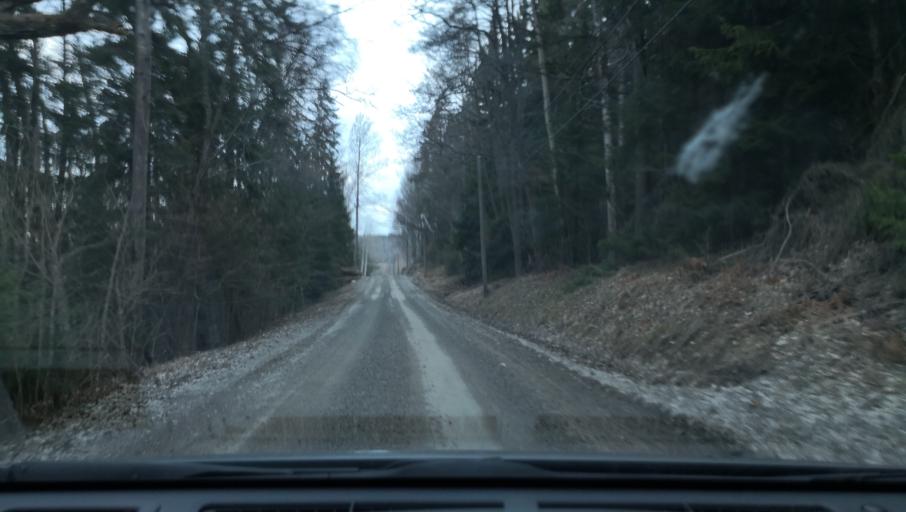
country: SE
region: Vaestmanland
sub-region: Kopings Kommun
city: Kolsva
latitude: 59.5965
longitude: 15.7165
